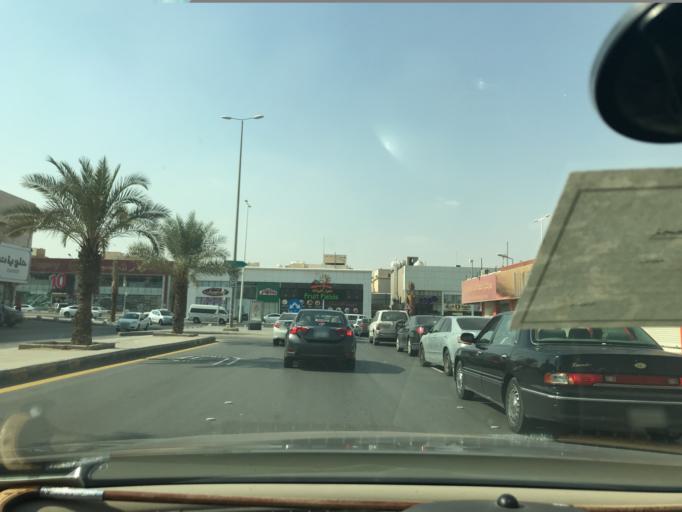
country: SA
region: Ar Riyad
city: Riyadh
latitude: 24.7439
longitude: 46.7565
